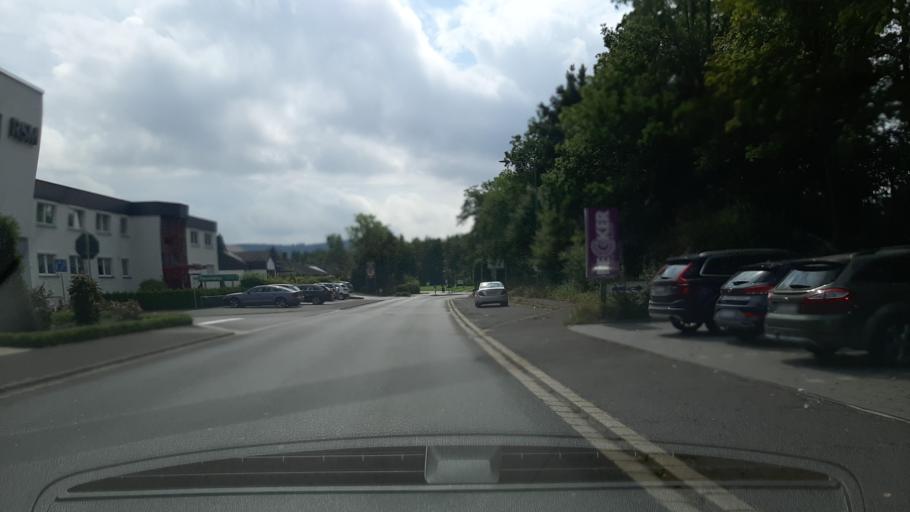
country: DE
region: Rheinland-Pfalz
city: Briedel
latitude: 50.0277
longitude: 7.1638
